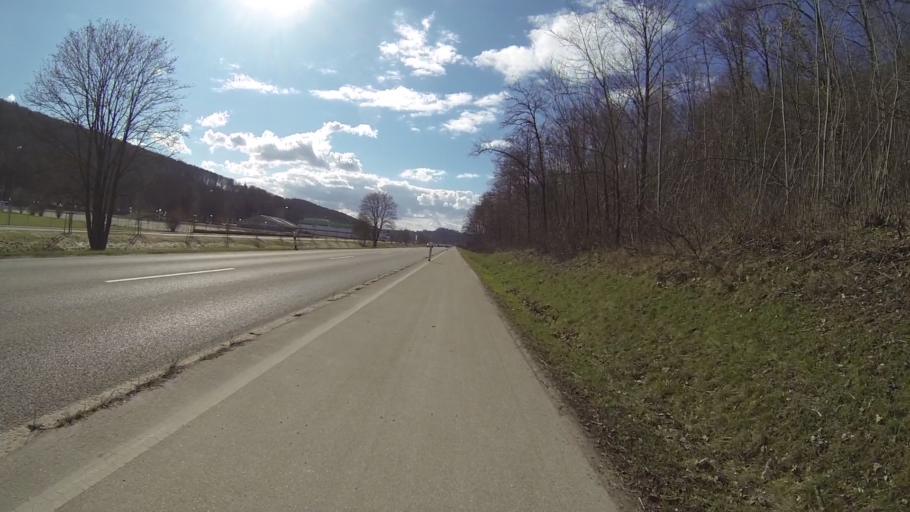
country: DE
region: Baden-Wuerttemberg
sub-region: Regierungsbezirk Stuttgart
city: Heidenheim an der Brenz
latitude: 48.6801
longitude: 10.1140
